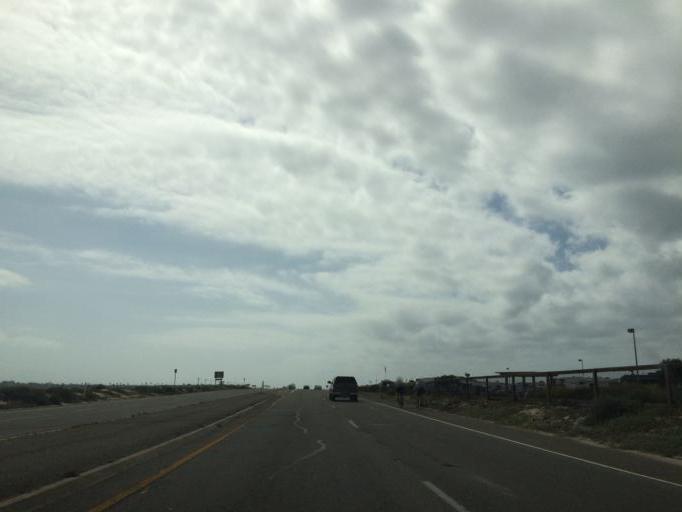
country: US
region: California
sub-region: Orange County
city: Huntington Beach
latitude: 33.6929
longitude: -118.0447
